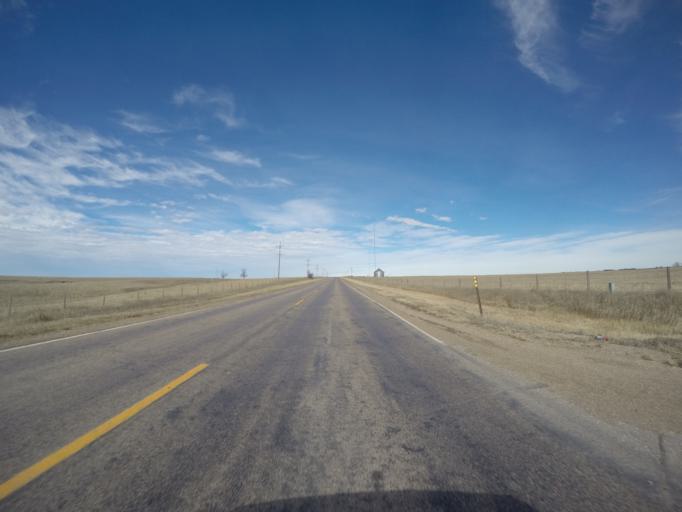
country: US
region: Nebraska
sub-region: Franklin County
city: Franklin
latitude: 40.1324
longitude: -98.9523
